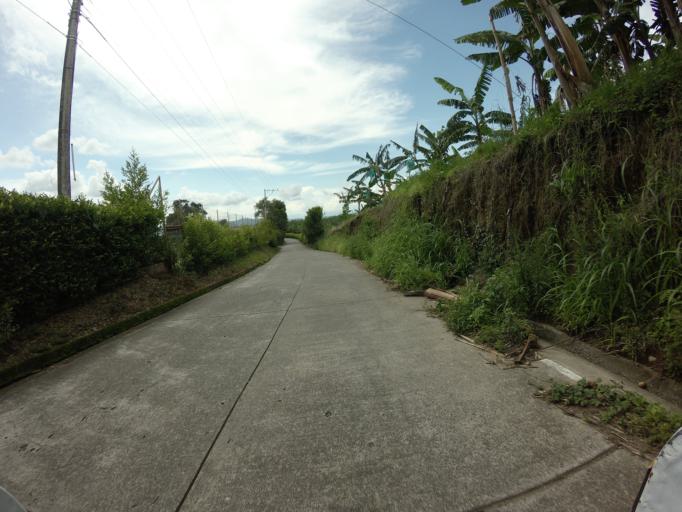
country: CO
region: Valle del Cauca
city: Ulloa
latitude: 4.7001
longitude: -75.7444
